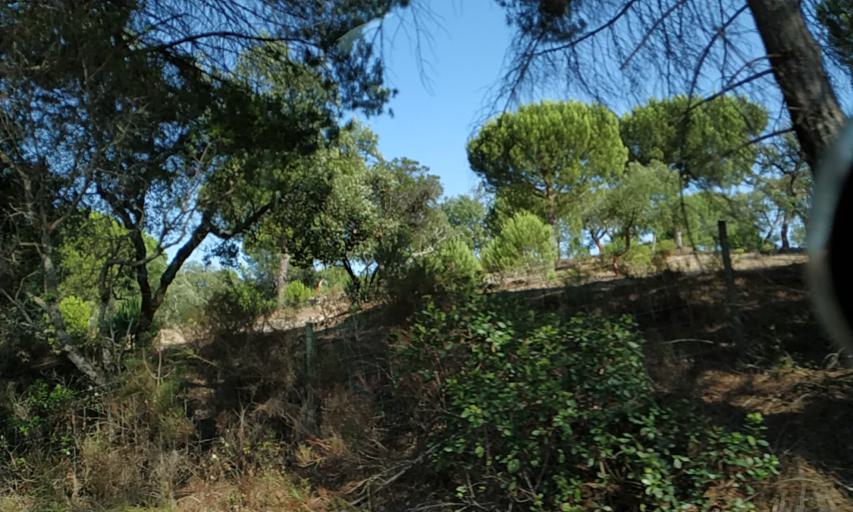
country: PT
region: Santarem
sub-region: Coruche
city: Coruche
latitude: 38.8638
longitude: -8.5436
